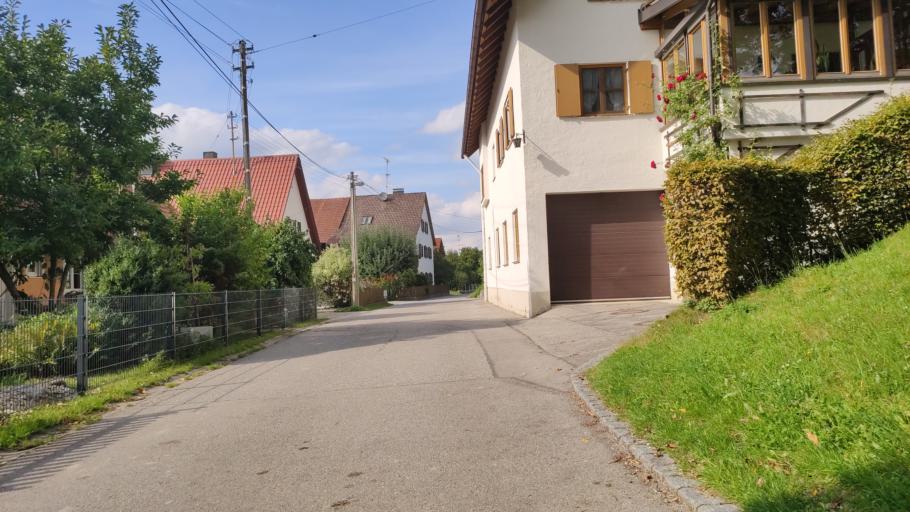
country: DE
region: Bavaria
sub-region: Upper Bavaria
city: Kaufering
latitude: 48.0937
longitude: 10.8744
